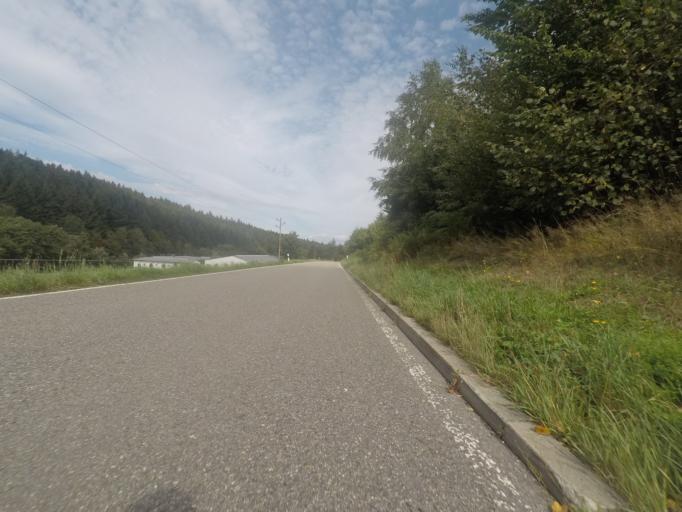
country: DE
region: Baden-Wuerttemberg
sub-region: Karlsruhe Region
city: Bad Herrenalb
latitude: 48.8454
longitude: 8.3899
